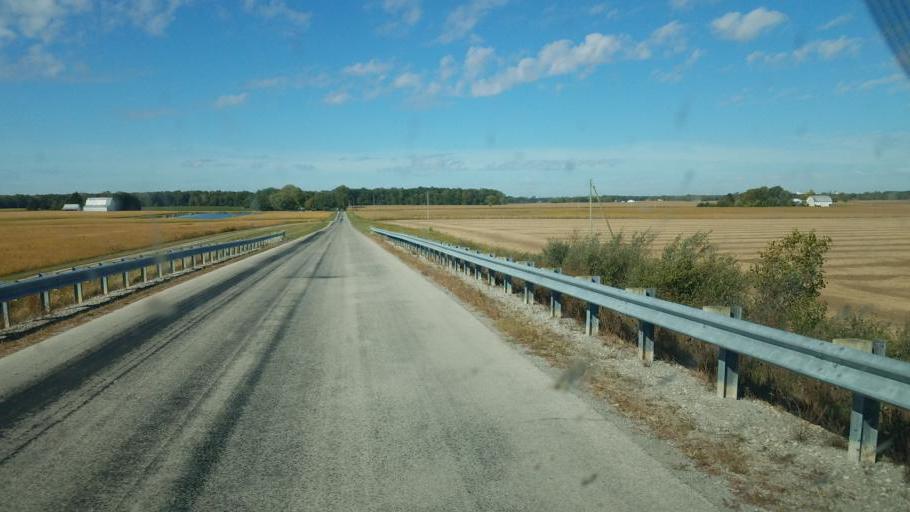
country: US
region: Ohio
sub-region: Wyandot County
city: Upper Sandusky
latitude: 40.8037
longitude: -83.2378
